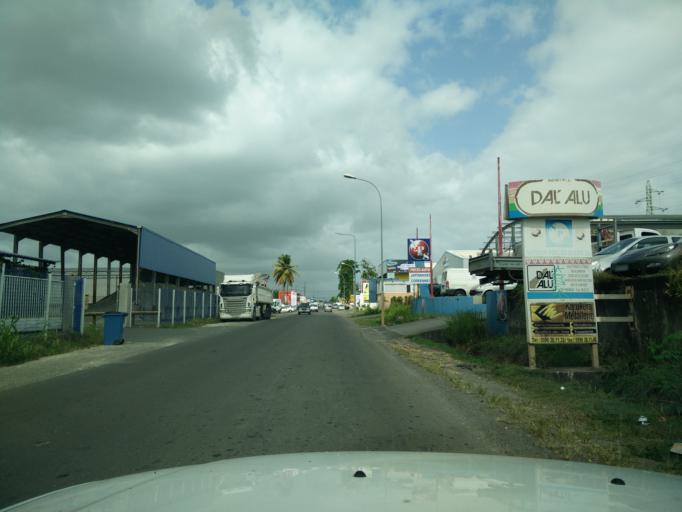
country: GP
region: Guadeloupe
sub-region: Guadeloupe
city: Pointe-a-Pitre
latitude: 16.2374
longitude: -61.5623
